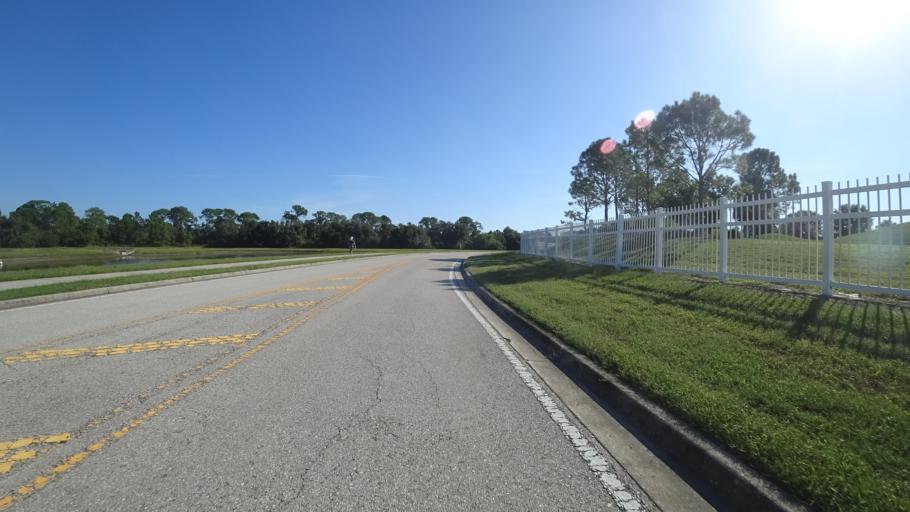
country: US
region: Florida
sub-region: Sarasota County
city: The Meadows
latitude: 27.4212
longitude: -82.4148
